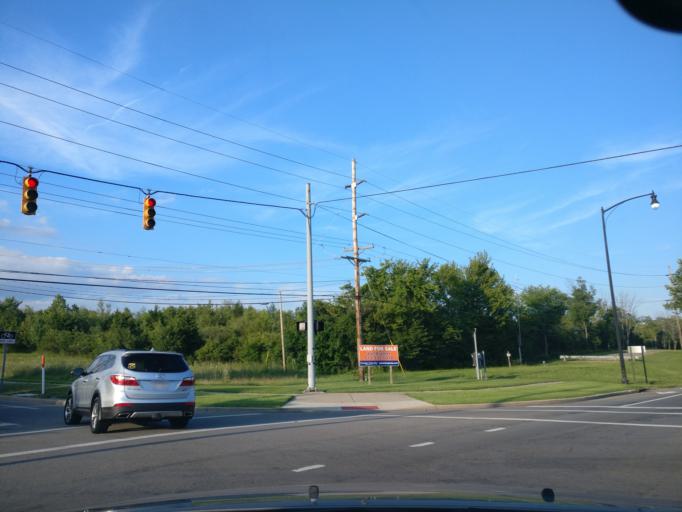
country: US
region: Ohio
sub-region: Warren County
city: Springboro
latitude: 39.5618
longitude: -84.2526
